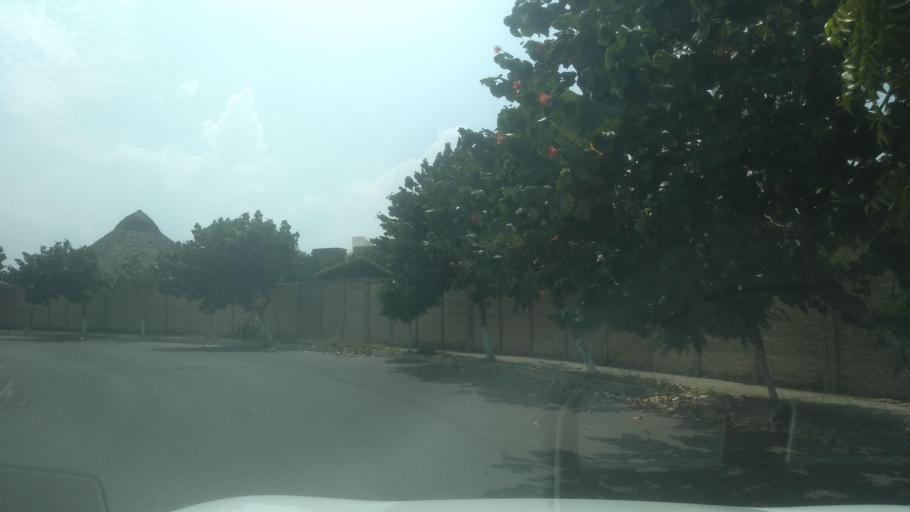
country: MX
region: Veracruz
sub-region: Veracruz
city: Las Amapolas
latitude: 19.1658
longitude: -96.1809
